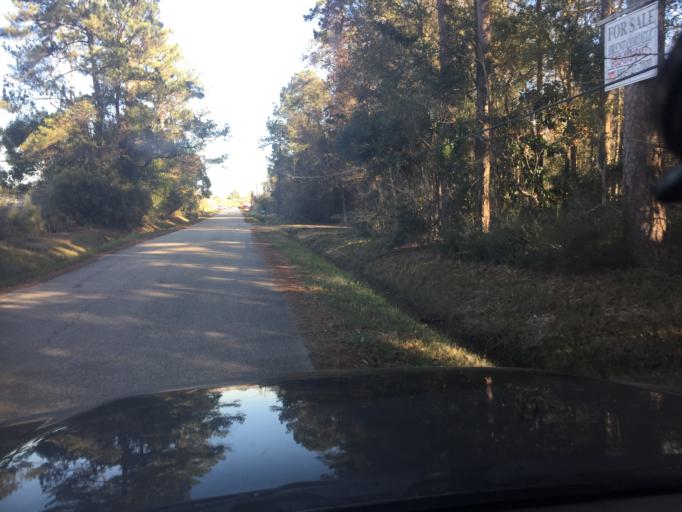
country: US
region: Louisiana
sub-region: Saint Tammany Parish
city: Slidell
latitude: 30.2427
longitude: -89.7635
